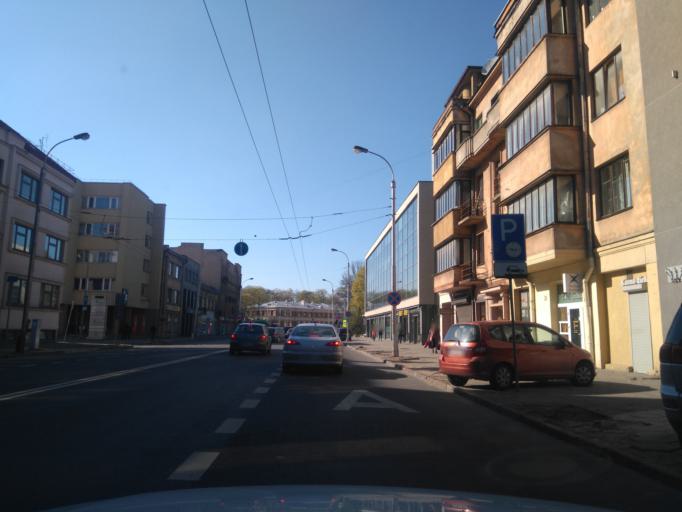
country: LT
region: Kauno apskritis
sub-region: Kaunas
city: Aleksotas
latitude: 54.8894
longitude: 23.9269
